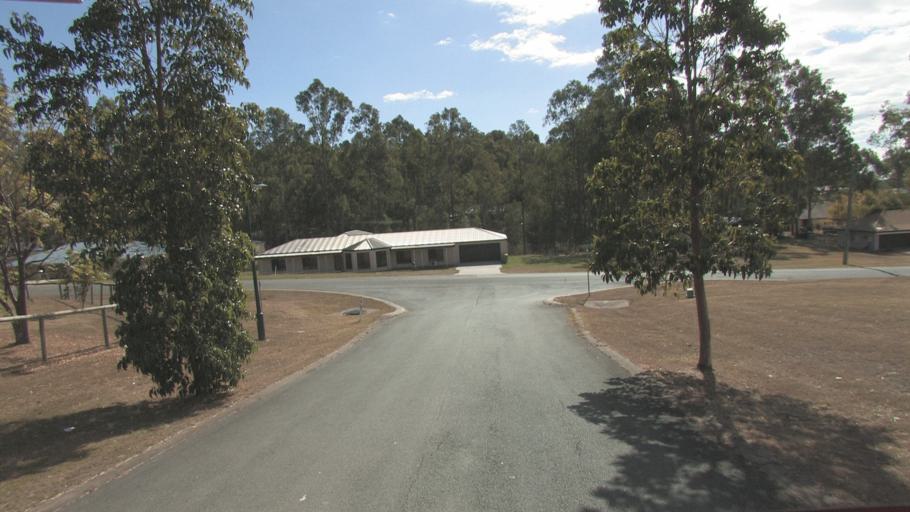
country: AU
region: Queensland
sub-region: Logan
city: Cedar Vale
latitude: -27.8748
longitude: 152.9977
